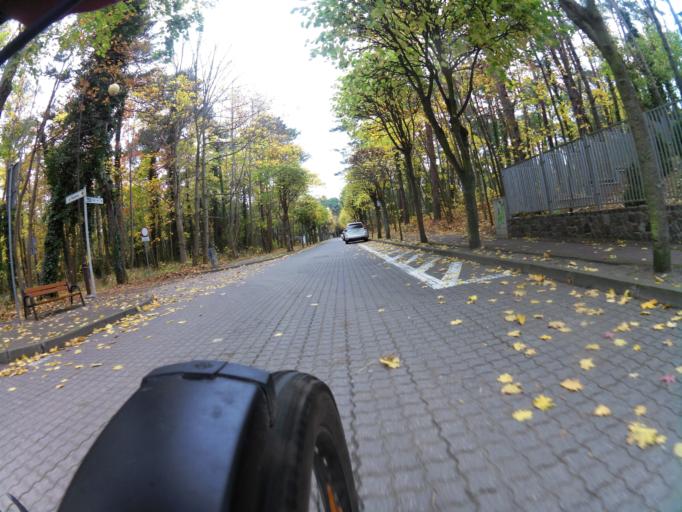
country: PL
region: Pomeranian Voivodeship
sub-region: Powiat pucki
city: Jastarnia
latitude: 54.6830
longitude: 18.7113
